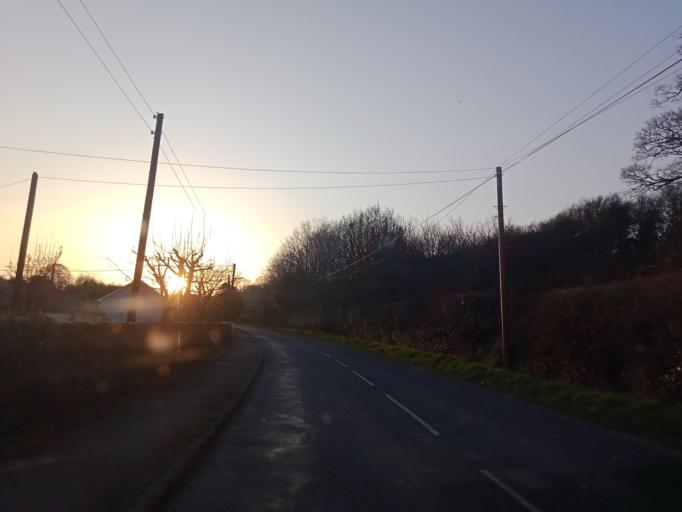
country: IE
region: Leinster
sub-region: Kilkenny
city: Castlecomer
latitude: 52.8080
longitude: -7.2129
